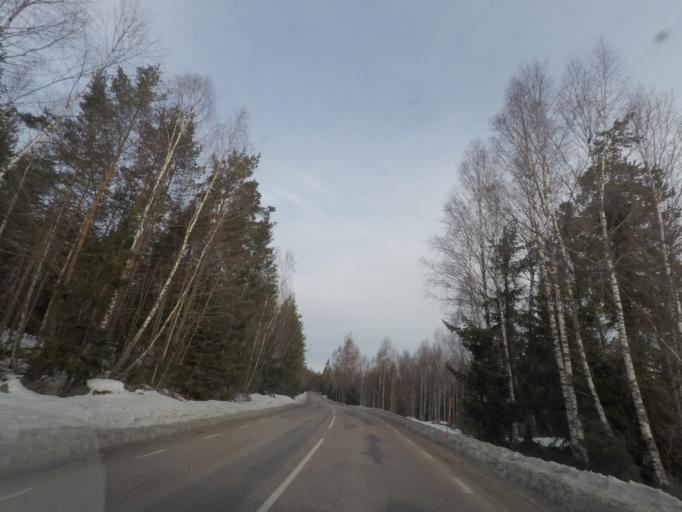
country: SE
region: Vaestmanland
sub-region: Surahammars Kommun
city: Surahammar
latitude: 59.7603
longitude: 16.2990
